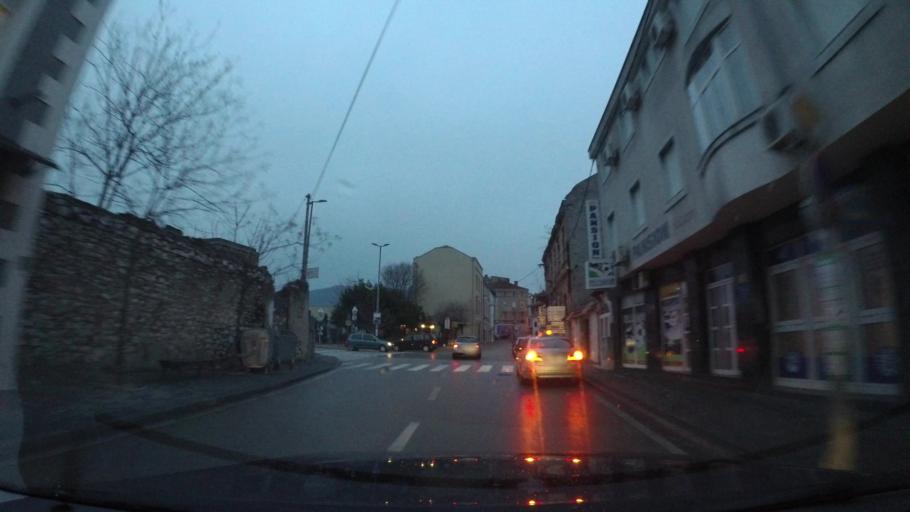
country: BA
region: Federation of Bosnia and Herzegovina
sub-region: Hercegovacko-Bosanski Kanton
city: Mostar
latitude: 43.3350
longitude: 17.8173
